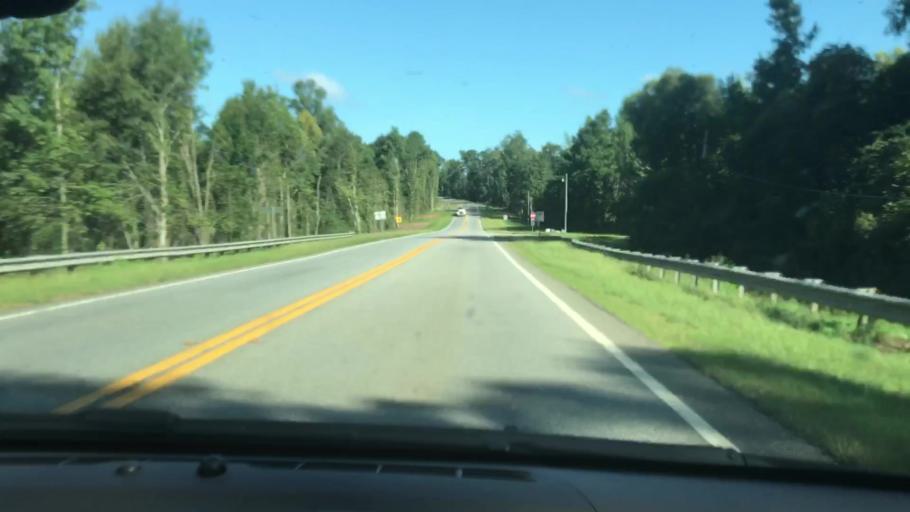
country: US
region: Georgia
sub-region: Quitman County
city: Georgetown
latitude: 31.8754
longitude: -85.0812
